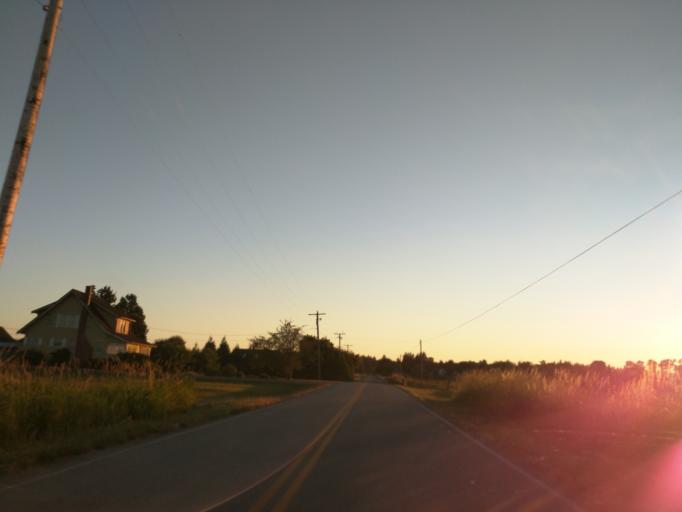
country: US
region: Washington
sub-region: Whatcom County
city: Sumas
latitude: 48.9785
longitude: -122.3103
